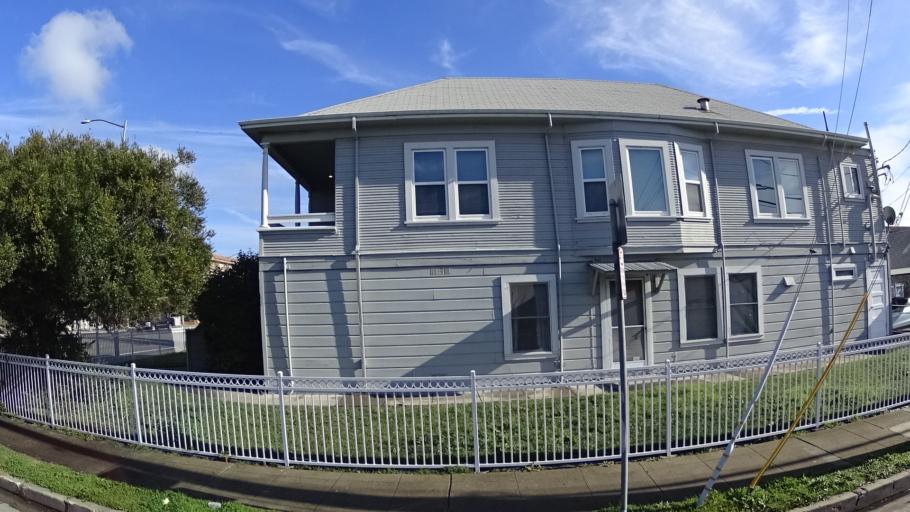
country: US
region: California
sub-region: Alameda County
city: Hayward
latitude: 37.6718
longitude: -122.0789
